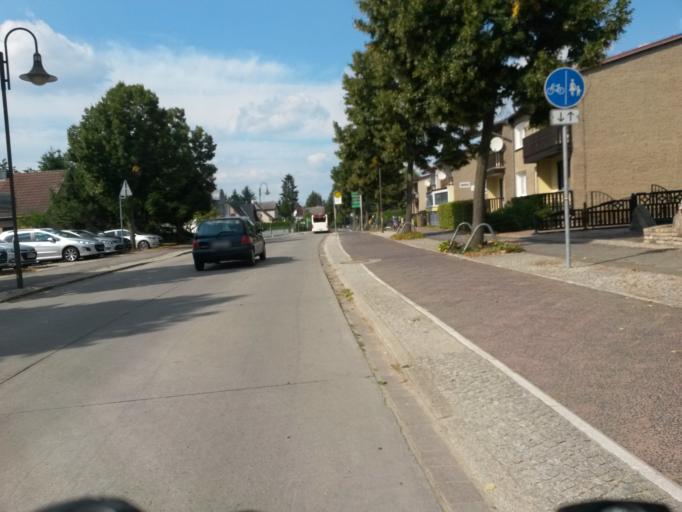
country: DE
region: Brandenburg
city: Templin
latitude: 53.1091
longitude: 13.5180
